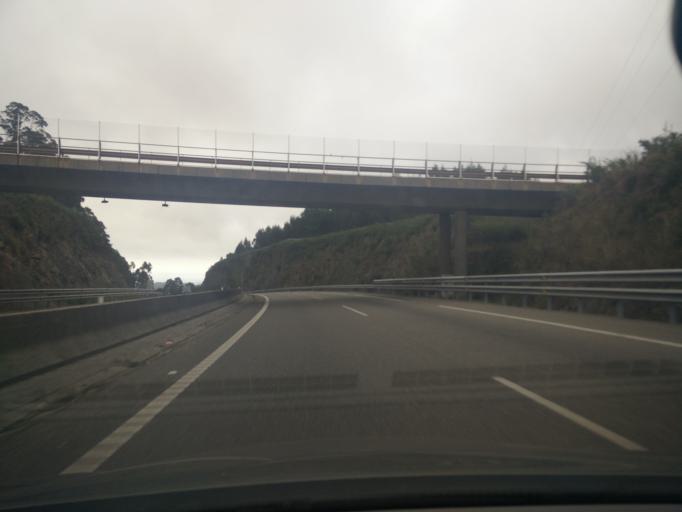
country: ES
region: Galicia
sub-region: Provincia da Coruna
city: Arteixo
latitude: 43.2773
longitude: -8.5268
